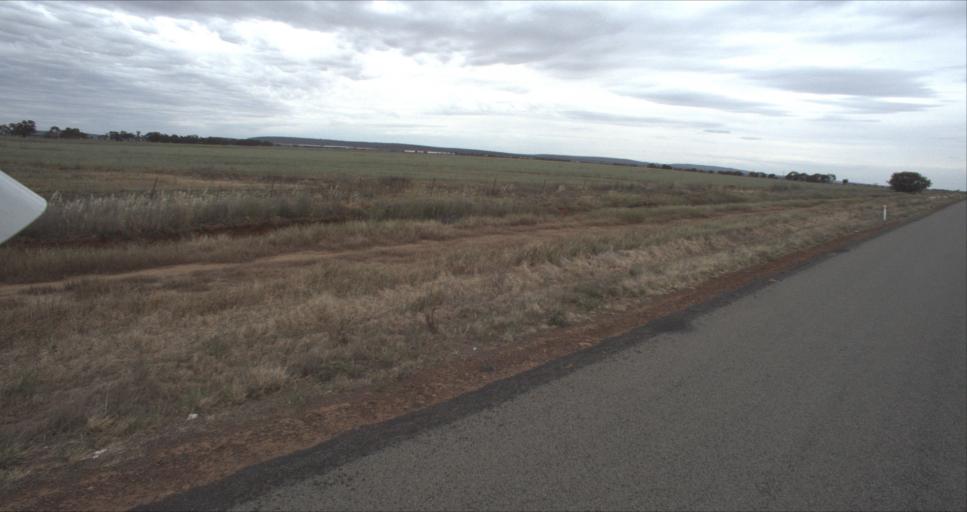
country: AU
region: New South Wales
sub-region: Leeton
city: Leeton
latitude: -34.4304
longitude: 146.3159
